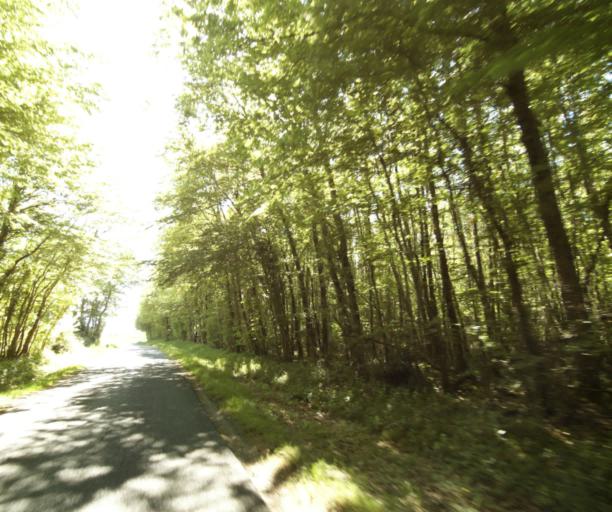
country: FR
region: Poitou-Charentes
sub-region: Departement de la Charente-Maritime
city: Bussac-sur-Charente
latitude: 45.8015
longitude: -0.6695
